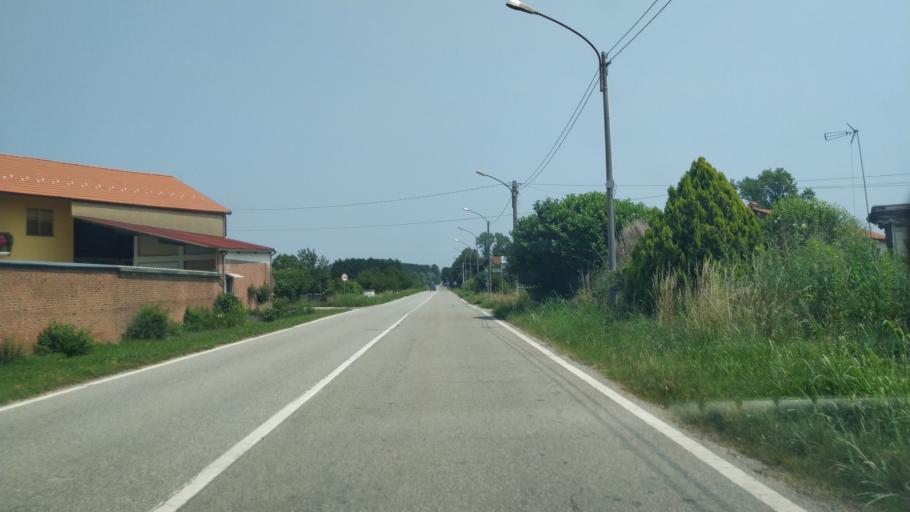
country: IT
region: Piedmont
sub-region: Provincia di Torino
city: Rondissone
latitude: 45.2501
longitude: 7.9656
